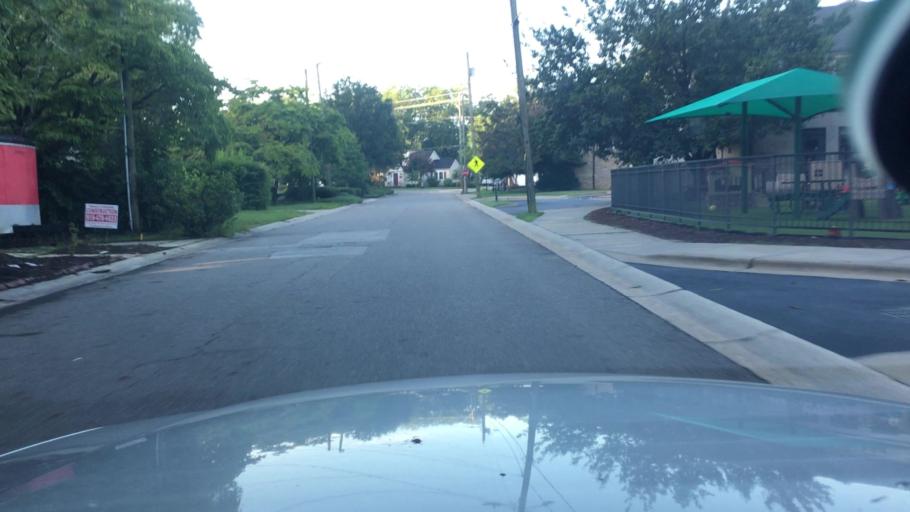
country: US
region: North Carolina
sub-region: Cumberland County
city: Fayetteville
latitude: 35.0633
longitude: -78.9086
